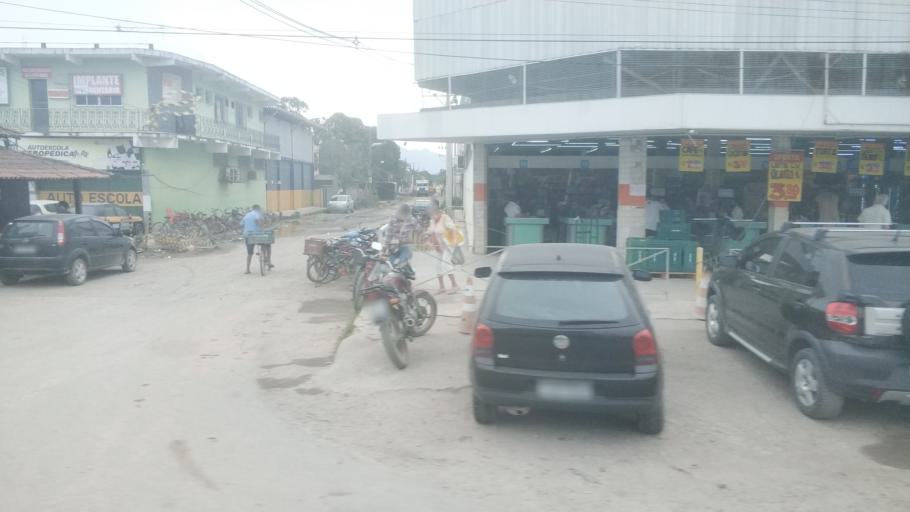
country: BR
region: Rio de Janeiro
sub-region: Seropedica
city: Seropedica
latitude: -22.8050
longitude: -43.6388
